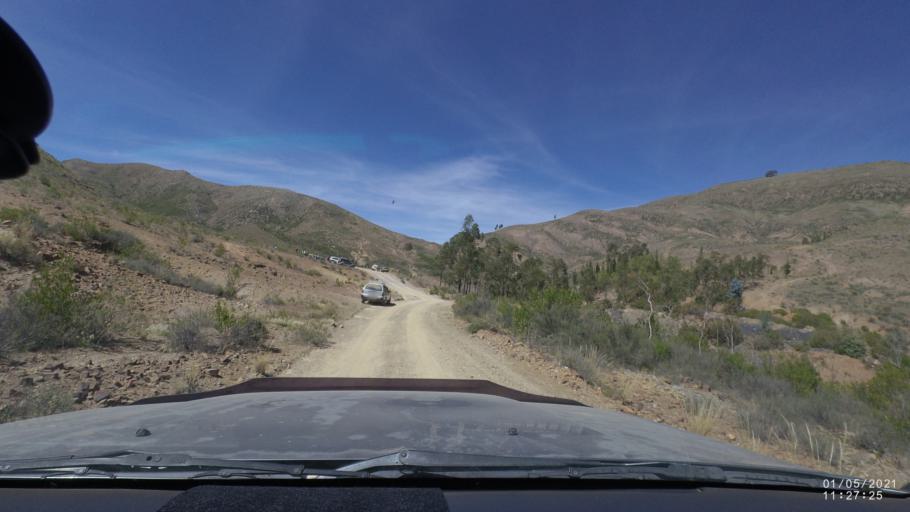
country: BO
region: Cochabamba
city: Tarata
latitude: -17.6570
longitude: -66.1314
